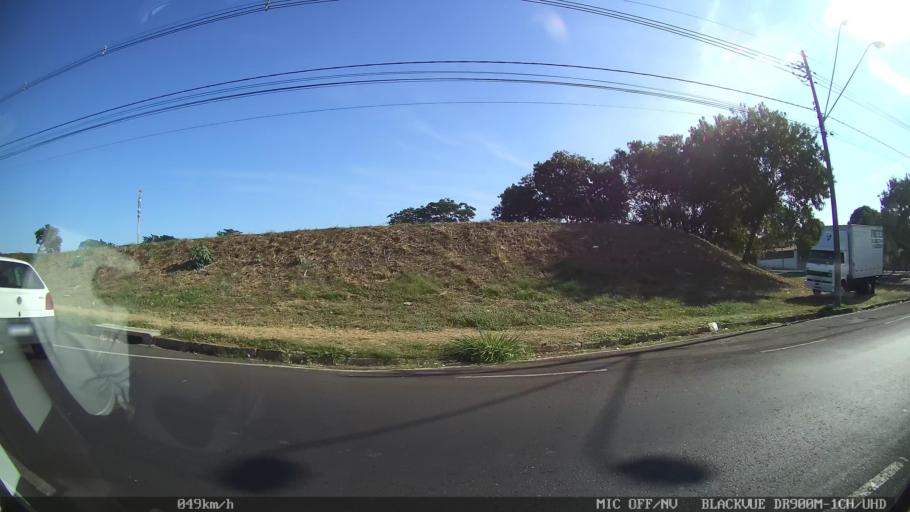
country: BR
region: Sao Paulo
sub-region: Sao Jose Do Rio Preto
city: Sao Jose do Rio Preto
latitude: -20.7677
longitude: -49.3863
